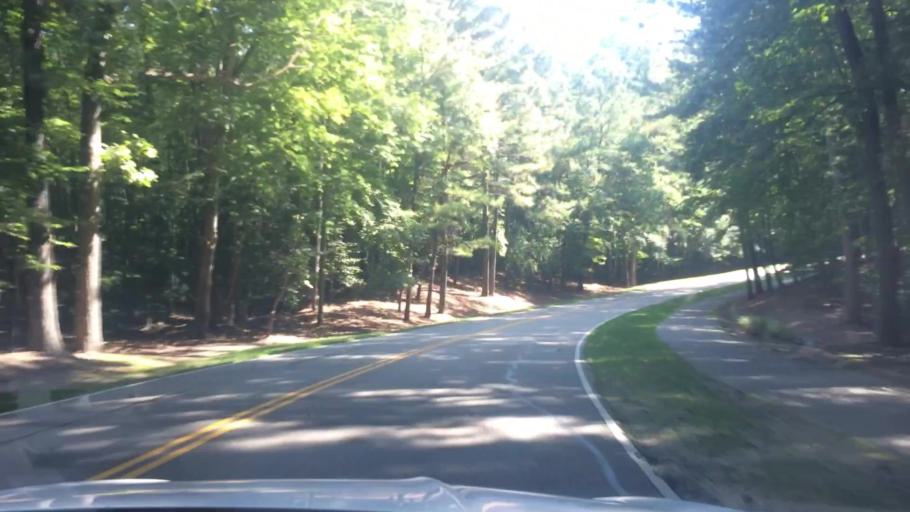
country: US
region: Virginia
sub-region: City of Williamsburg
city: Williamsburg
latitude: 37.2448
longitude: -76.6750
